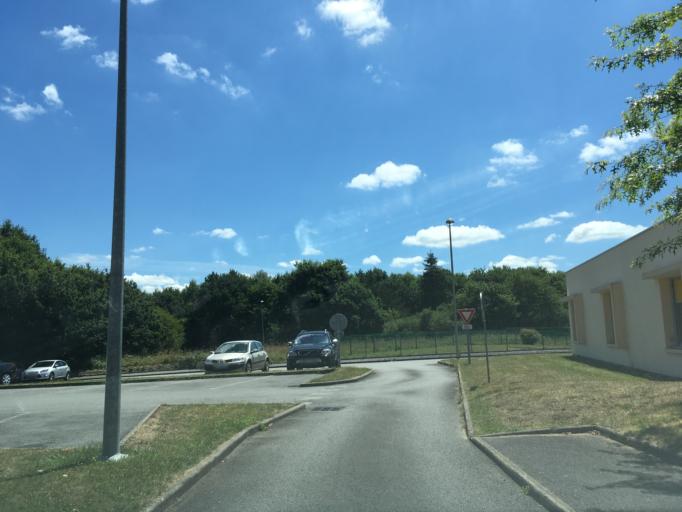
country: FR
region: Brittany
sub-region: Departement du Finistere
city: Quimper
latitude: 47.9769
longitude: -4.0827
